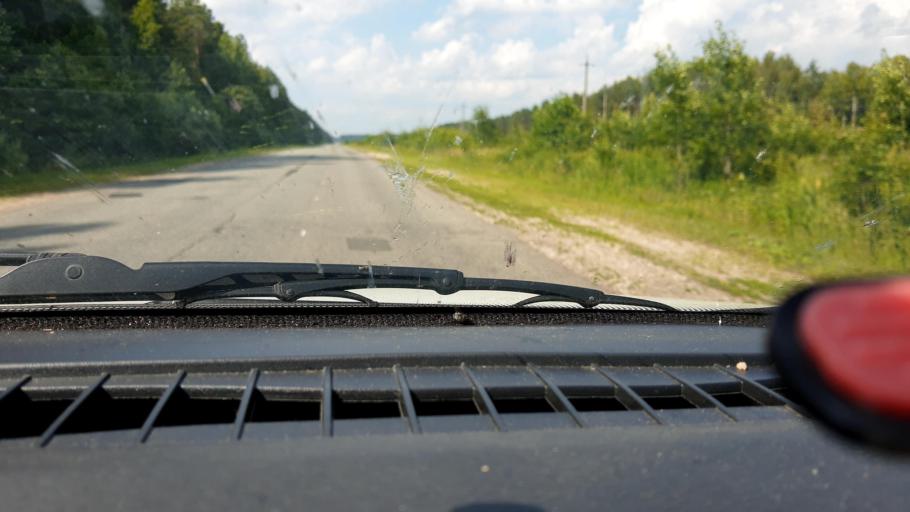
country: RU
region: Nizjnij Novgorod
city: Prudy
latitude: 57.4516
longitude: 46.0509
